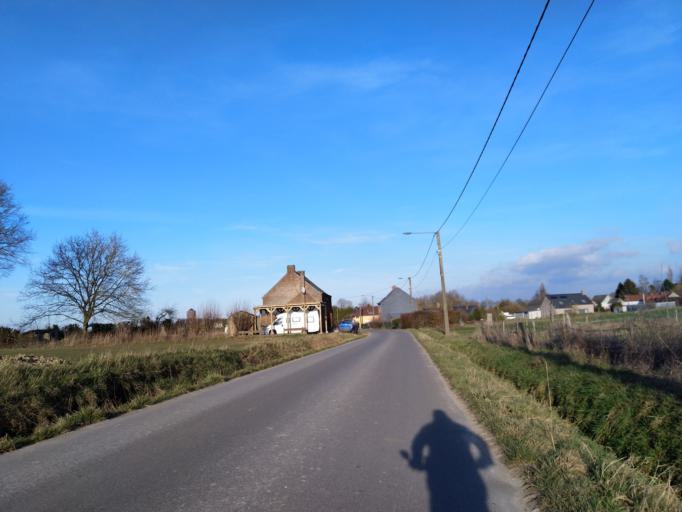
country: FR
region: Nord-Pas-de-Calais
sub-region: Departement du Nord
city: Feignies
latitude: 50.3335
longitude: 3.8954
